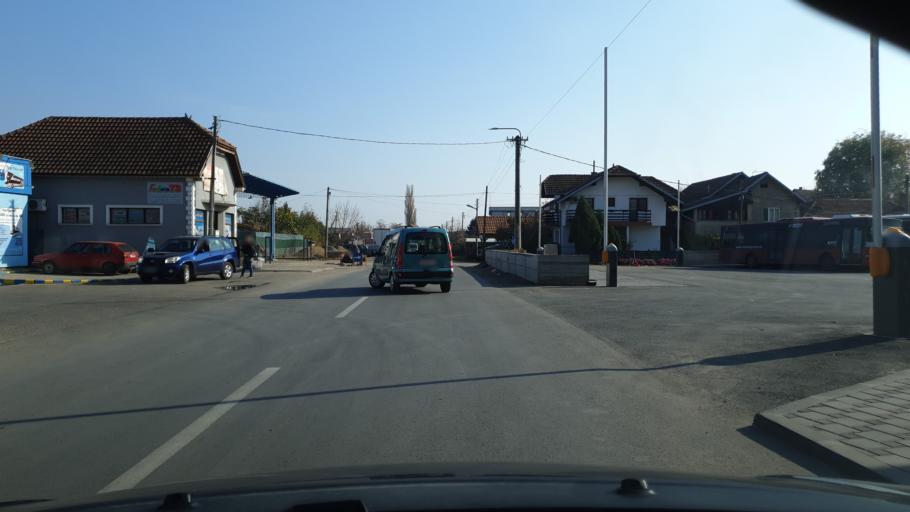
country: RS
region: Central Serbia
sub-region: Borski Okrug
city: Negotin
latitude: 44.2284
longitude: 22.5399
